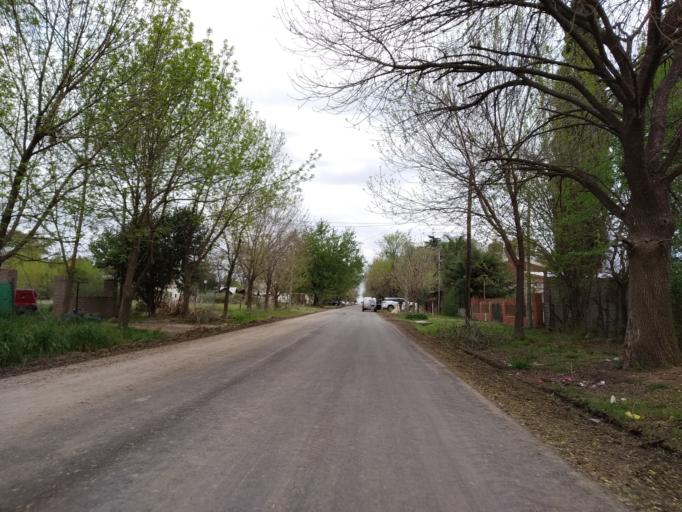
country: AR
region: Santa Fe
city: Funes
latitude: -32.9203
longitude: -60.8512
